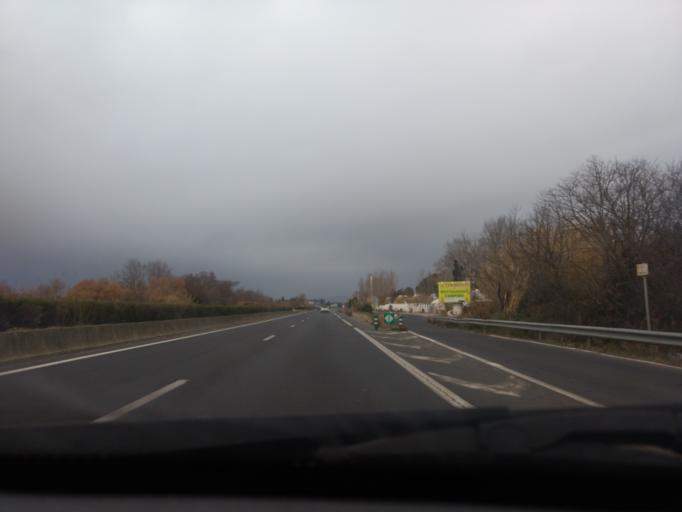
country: FR
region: Languedoc-Roussillon
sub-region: Departement de l'Herault
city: Lattes
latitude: 43.5473
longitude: 3.8949
